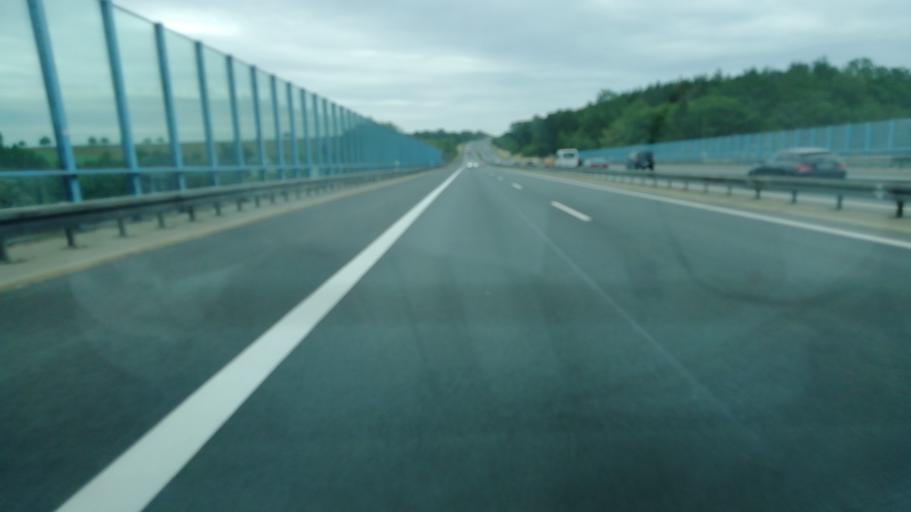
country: DE
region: Saxony
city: Neuensalz
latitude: 50.5169
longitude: 12.2279
